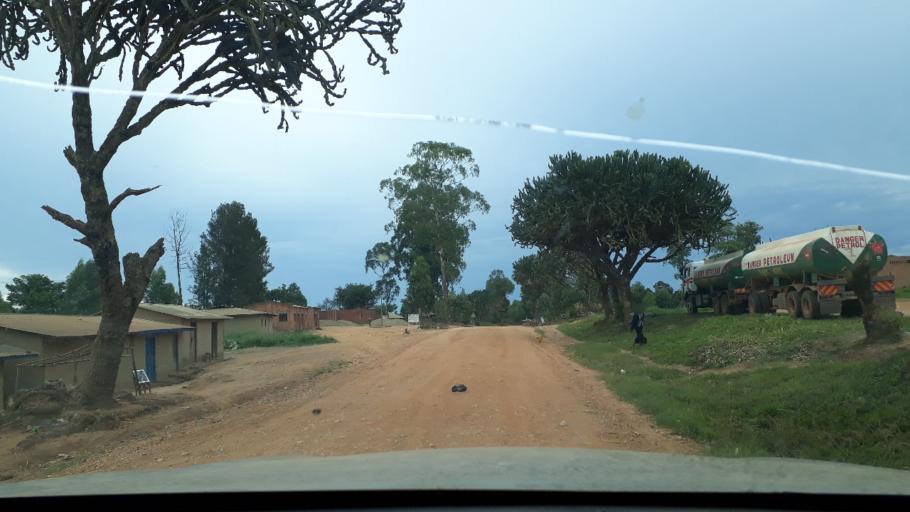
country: CD
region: Eastern Province
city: Bunia
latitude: 1.8509
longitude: 30.4797
